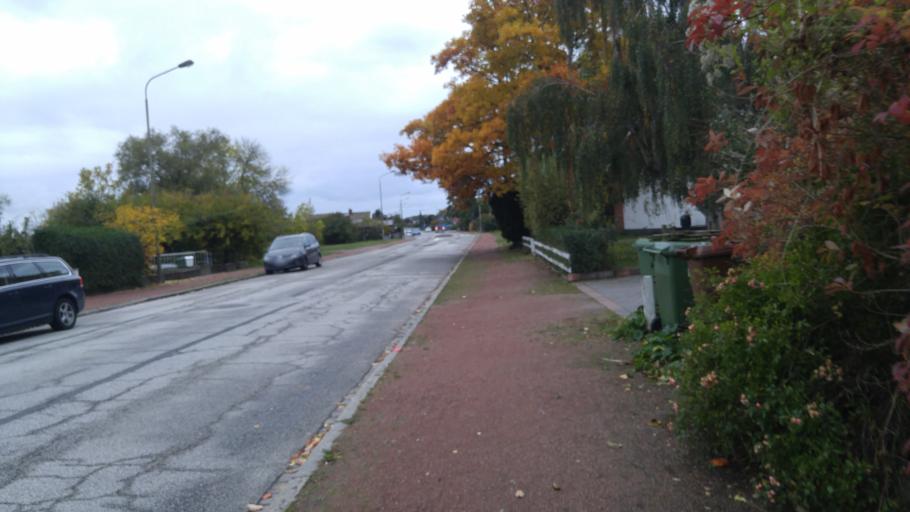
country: SE
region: Skane
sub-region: Malmo
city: Bunkeflostrand
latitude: 55.5761
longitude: 12.9511
